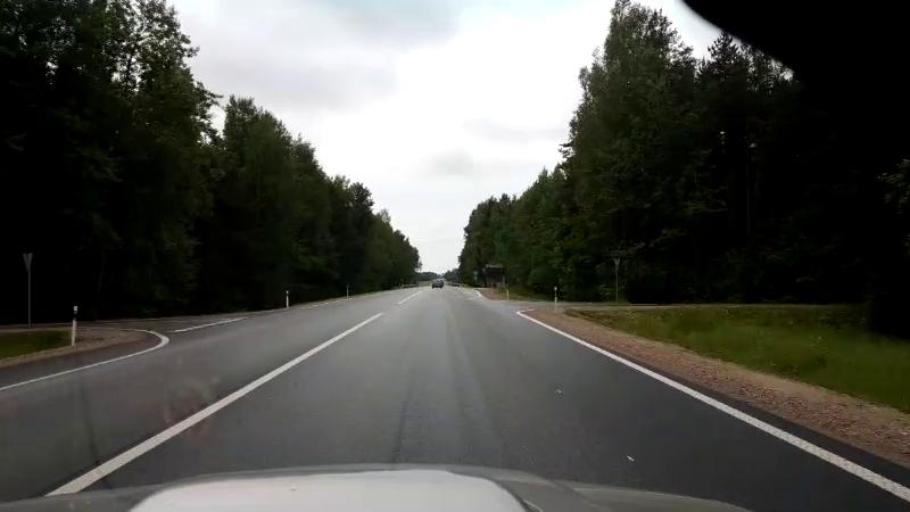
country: LV
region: Lecava
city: Iecava
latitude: 56.6632
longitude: 24.2329
